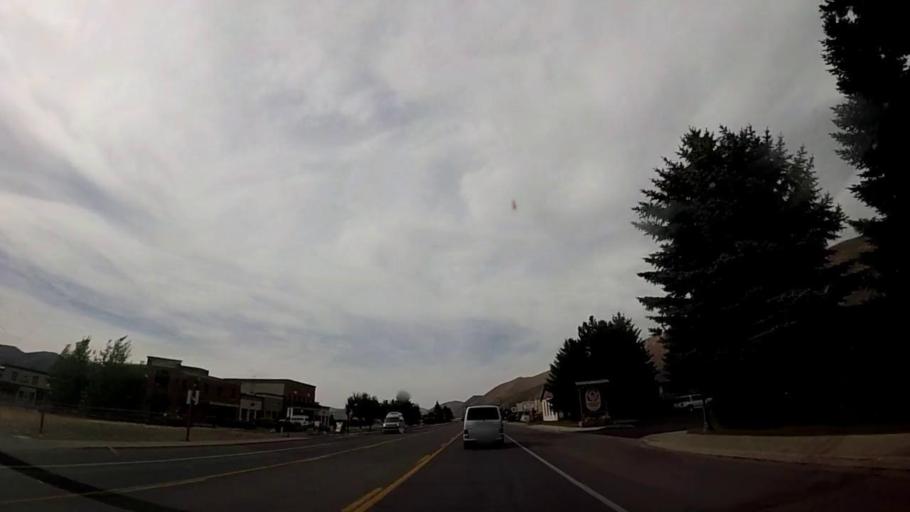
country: US
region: Idaho
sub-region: Blaine County
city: Bellevue
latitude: 43.4715
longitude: -114.2641
